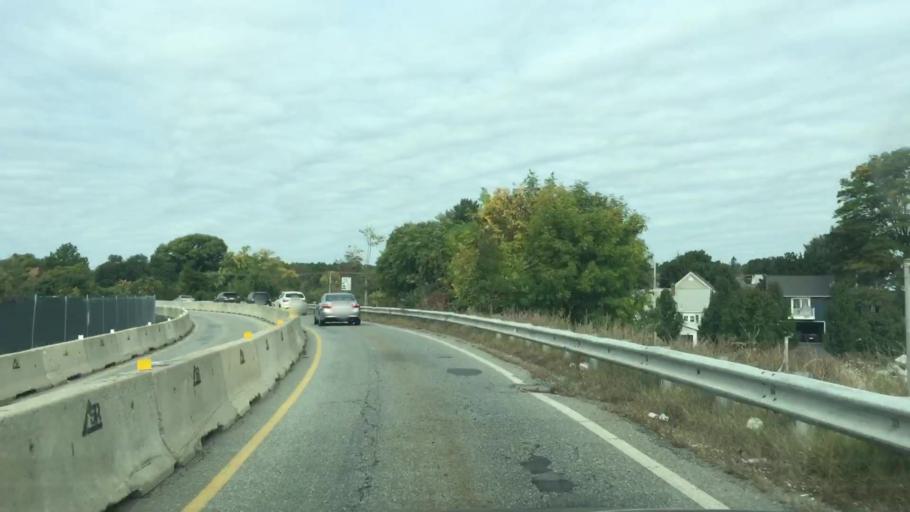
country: US
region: Massachusetts
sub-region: Middlesex County
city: Dracut
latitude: 42.6585
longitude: -71.3166
